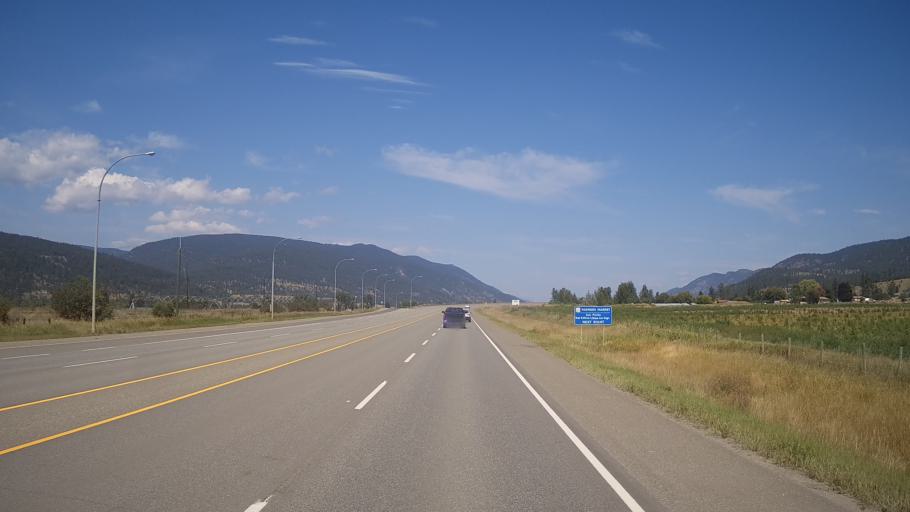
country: CA
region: British Columbia
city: Kamloops
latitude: 50.8535
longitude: -120.2739
